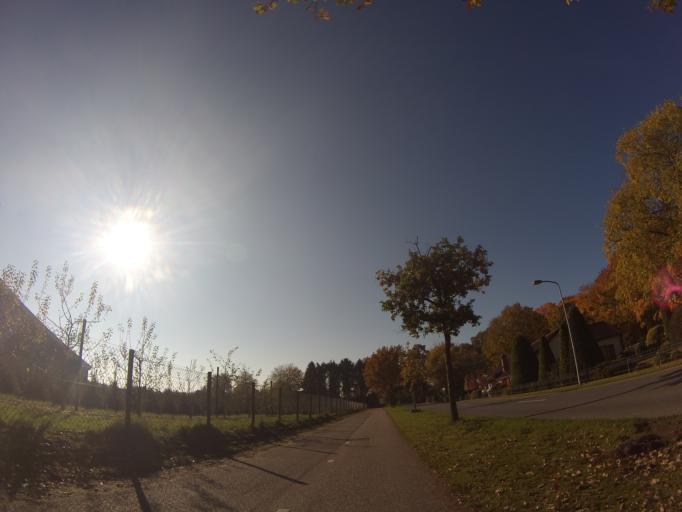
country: NL
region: Utrecht
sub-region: Gemeente Utrechtse Heuvelrug
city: Driebergen-Rijsenburg
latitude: 52.0613
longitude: 5.2511
